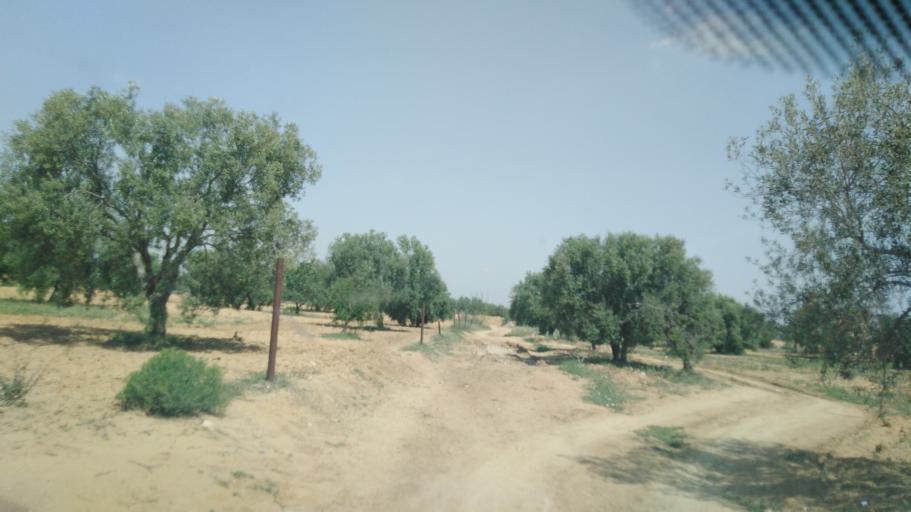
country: TN
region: Safaqis
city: Sfax
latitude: 34.7333
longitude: 10.5745
